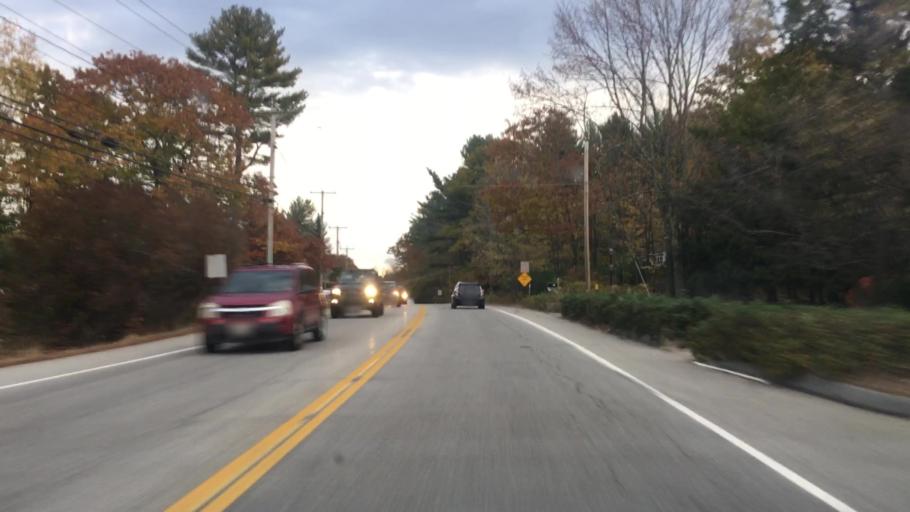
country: US
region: Maine
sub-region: York County
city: Biddeford
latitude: 43.4739
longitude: -70.5262
